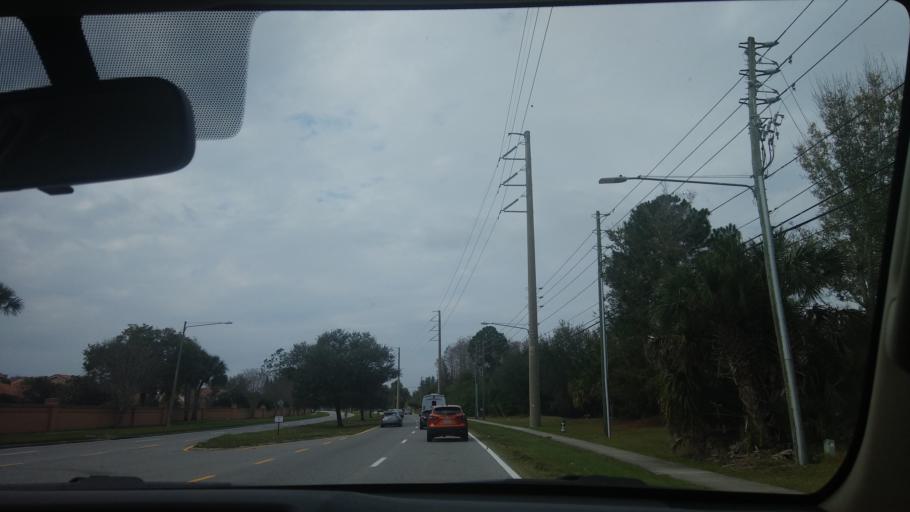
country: US
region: Florida
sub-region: Orange County
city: Williamsburg
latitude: 28.4103
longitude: -81.4403
